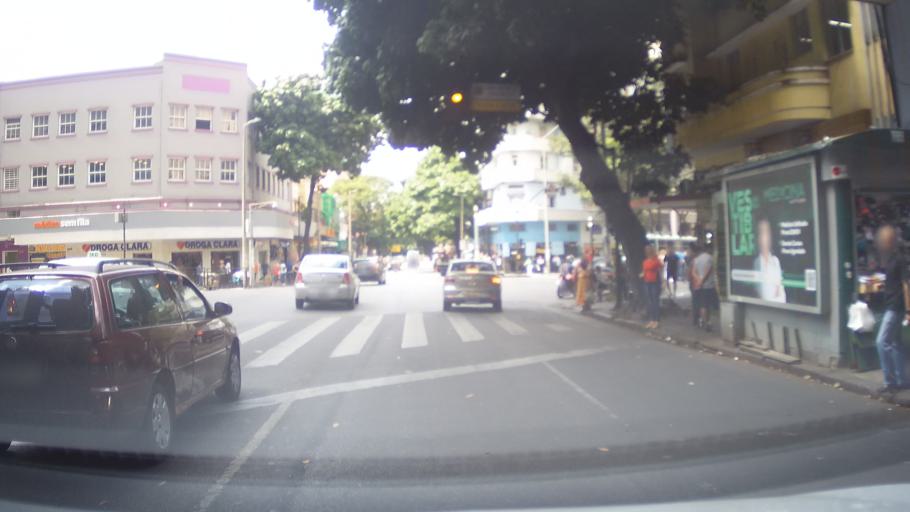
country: BR
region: Minas Gerais
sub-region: Belo Horizonte
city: Belo Horizonte
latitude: -19.9188
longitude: -43.9371
